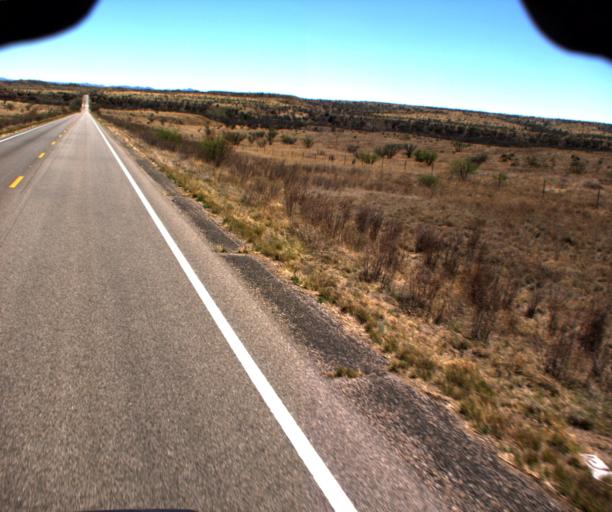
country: US
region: Arizona
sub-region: Pima County
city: Corona de Tucson
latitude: 31.7445
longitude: -110.6677
